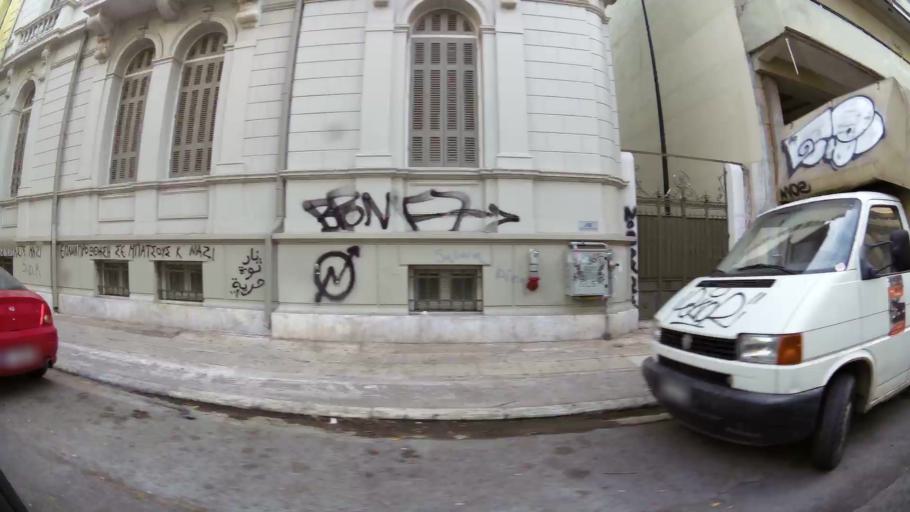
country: GR
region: Attica
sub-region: Nomarchia Athinas
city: Kipseli
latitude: 37.9932
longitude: 23.7271
